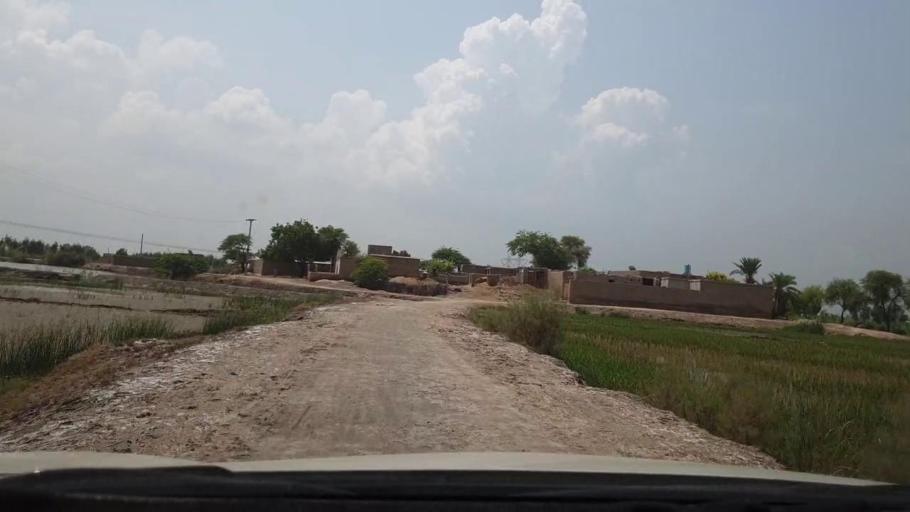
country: PK
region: Sindh
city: New Badah
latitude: 27.3887
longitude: 68.0420
